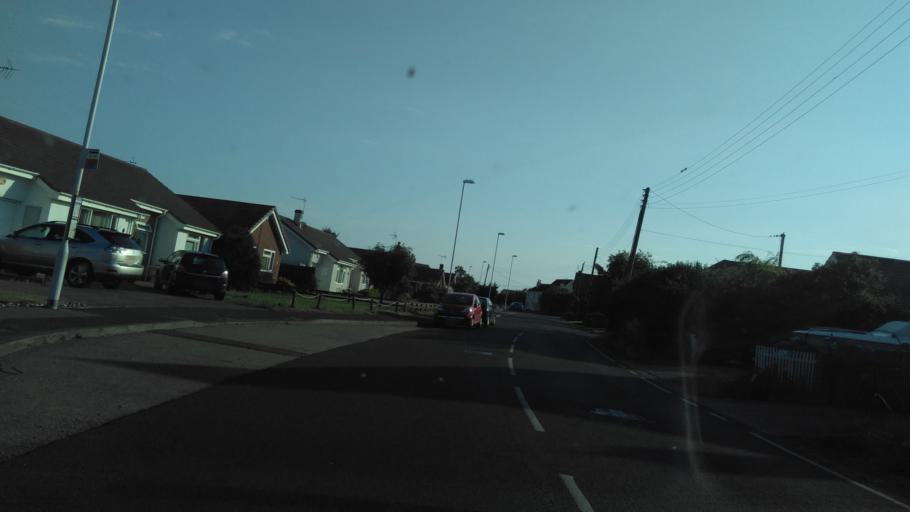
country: GB
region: England
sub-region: Kent
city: Whitstable
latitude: 51.3459
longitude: 1.0021
